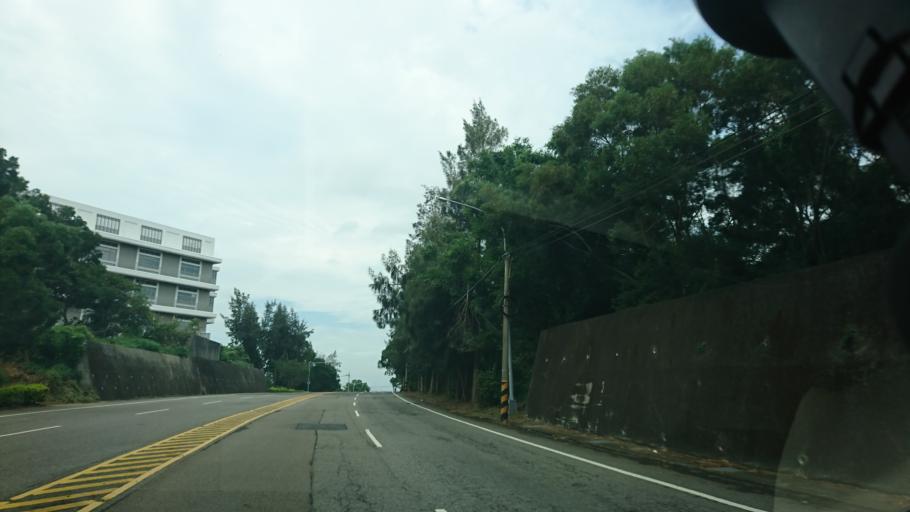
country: TW
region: Taiwan
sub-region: Miaoli
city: Miaoli
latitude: 24.5184
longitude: 120.7883
